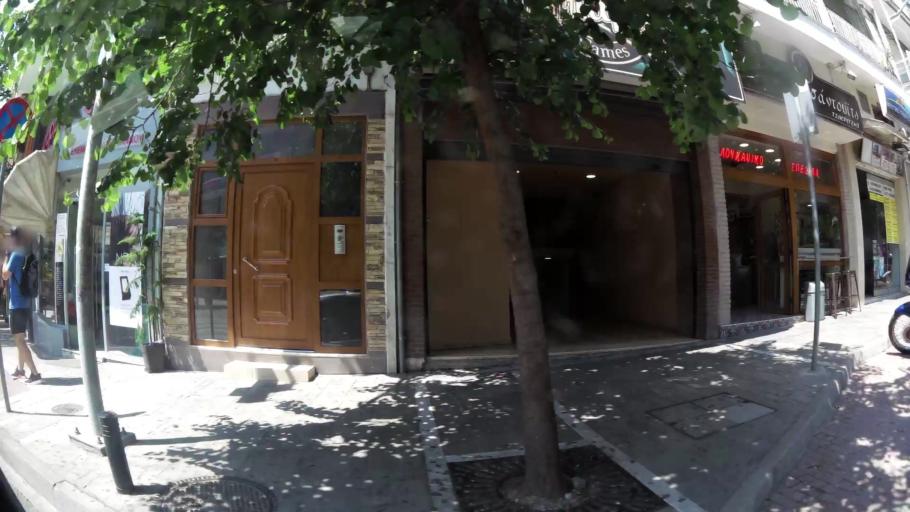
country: GR
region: West Macedonia
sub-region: Nomos Kozanis
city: Kozani
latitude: 40.3016
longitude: 21.7859
